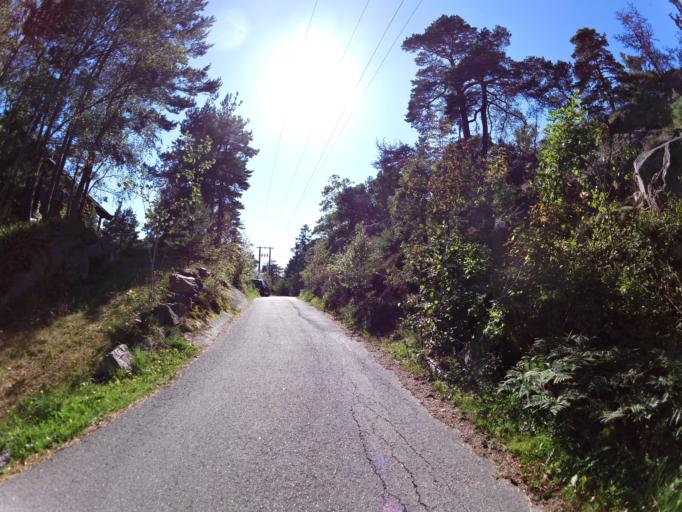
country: NO
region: Ostfold
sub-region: Fredrikstad
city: Fredrikstad
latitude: 59.1686
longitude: 10.8419
